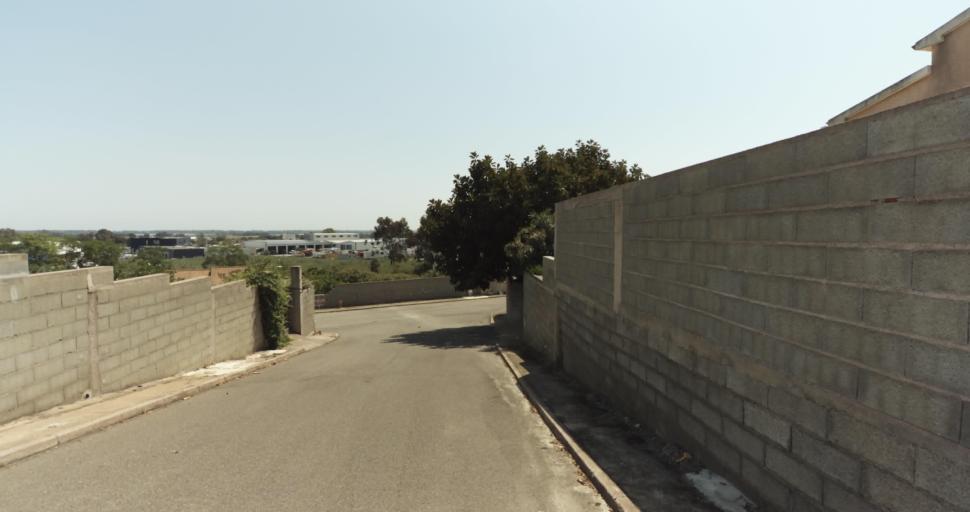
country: FR
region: Corsica
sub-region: Departement de la Haute-Corse
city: Biguglia
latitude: 42.6048
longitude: 9.4329
